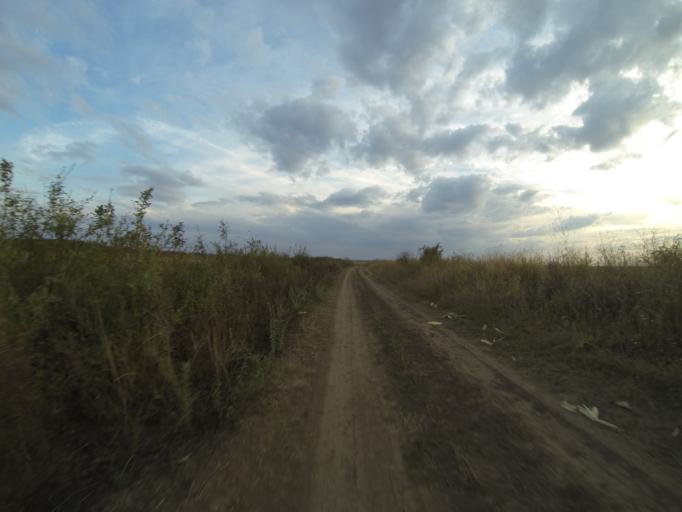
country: RO
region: Dolj
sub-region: Comuna Ceratu
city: Ceratu
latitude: 44.0960
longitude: 23.6693
